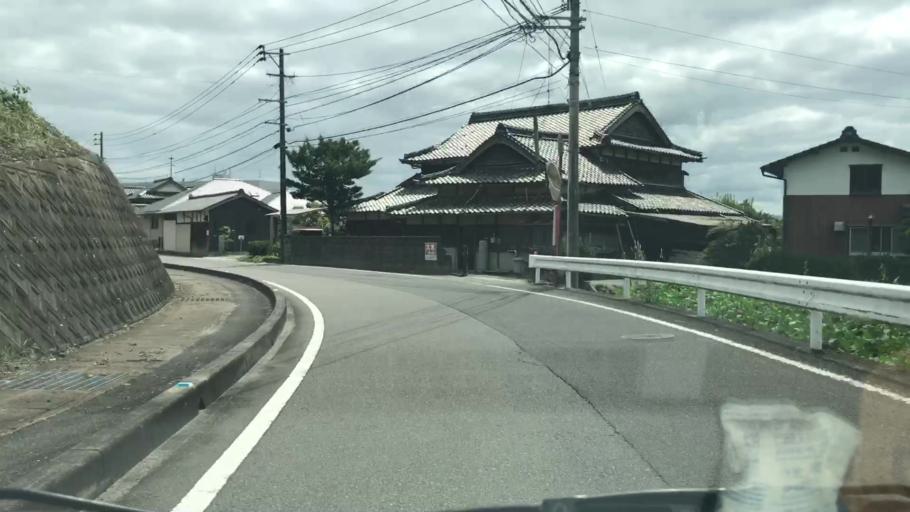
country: JP
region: Saga Prefecture
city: Kashima
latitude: 33.2230
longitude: 130.1570
